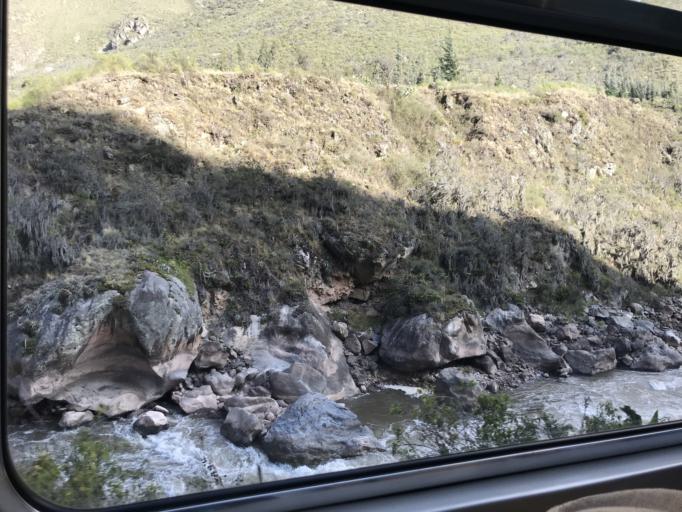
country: PE
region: Cusco
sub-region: Provincia de Urubamba
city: Ollantaytambo
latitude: -13.2226
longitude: -72.3954
